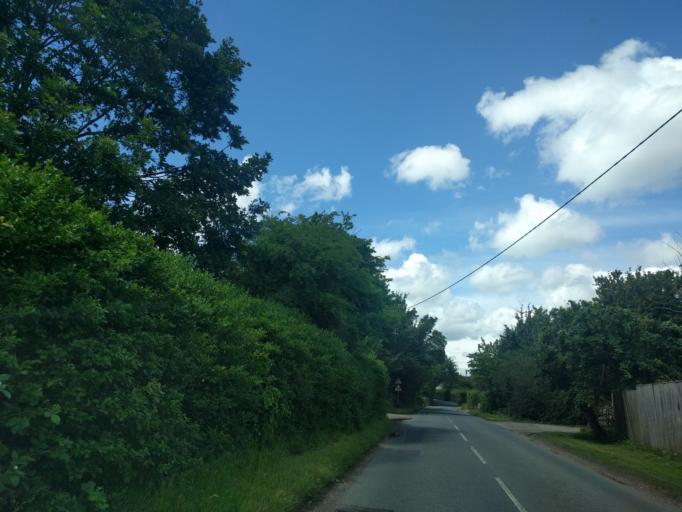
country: GB
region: England
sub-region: West Berkshire
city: Kintbury
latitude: 51.3866
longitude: -1.4070
